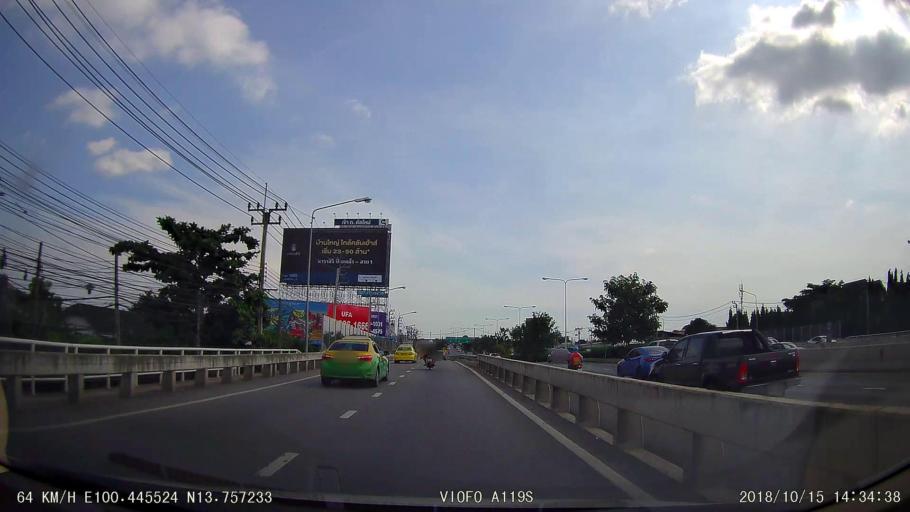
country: TH
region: Bangkok
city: Taling Chan
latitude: 13.7569
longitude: 100.4456
